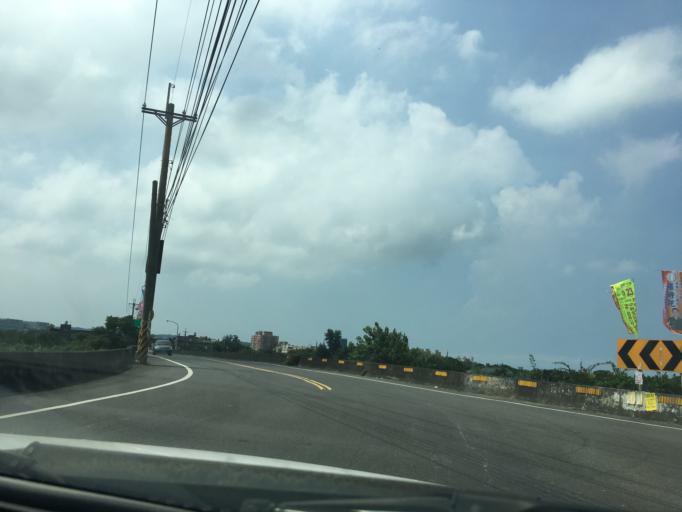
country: TW
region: Taiwan
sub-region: Hsinchu
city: Zhubei
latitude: 24.9078
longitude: 120.9966
